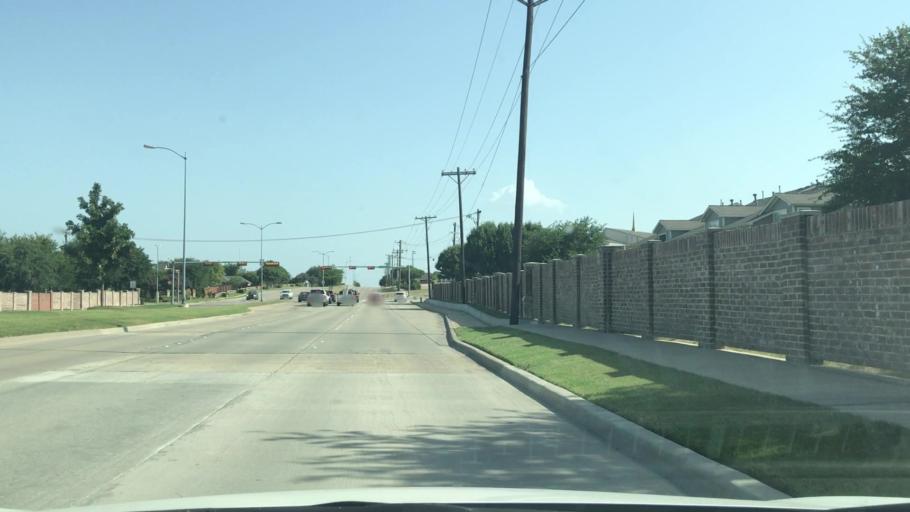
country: US
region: Texas
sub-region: Collin County
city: Allen
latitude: 33.1134
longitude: -96.7509
